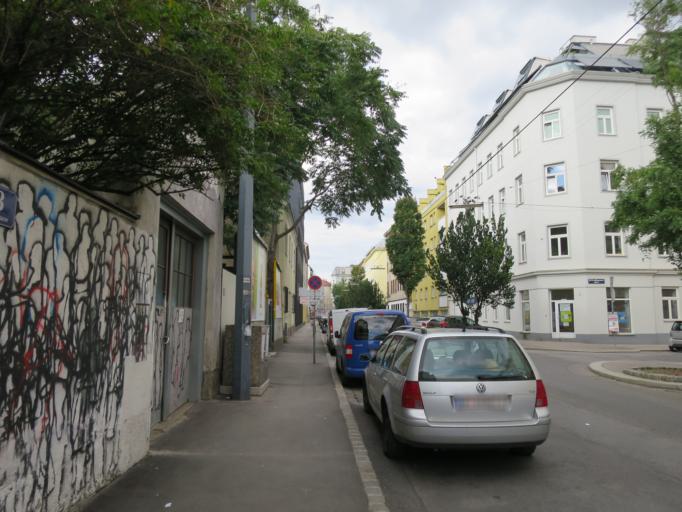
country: AT
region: Vienna
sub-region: Wien Stadt
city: Vienna
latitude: 48.2127
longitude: 16.3336
